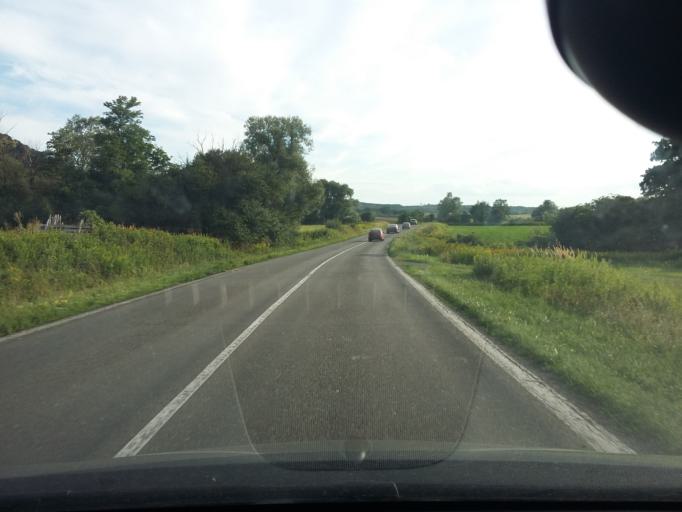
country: SK
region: Bratislavsky
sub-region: Okres Malacky
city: Malacky
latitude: 48.3807
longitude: 17.1517
